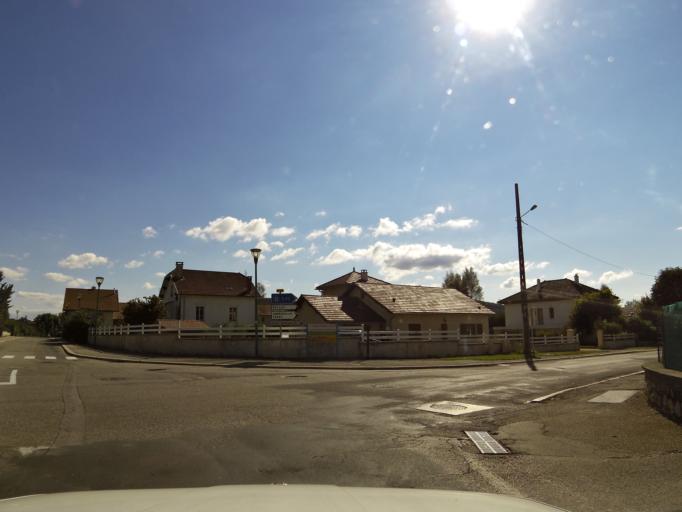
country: FR
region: Rhone-Alpes
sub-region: Departement de l'Ain
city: Hauteville-Lompnes
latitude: 45.9747
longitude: 5.5958
